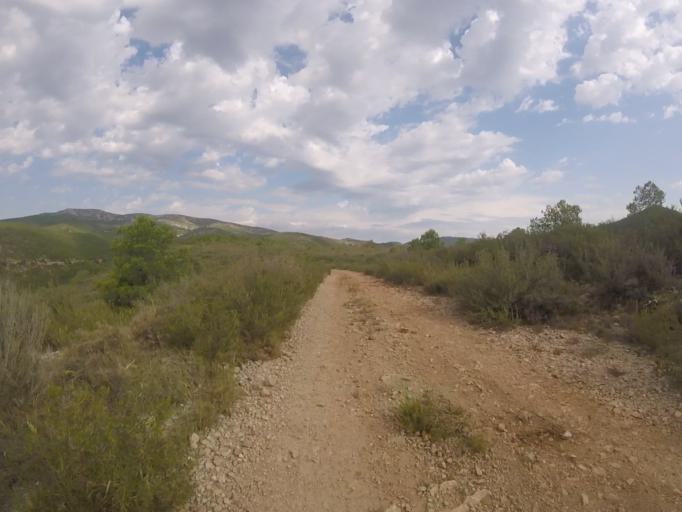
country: ES
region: Valencia
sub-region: Provincia de Castello
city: Alcala de Xivert
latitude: 40.3842
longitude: 0.2111
